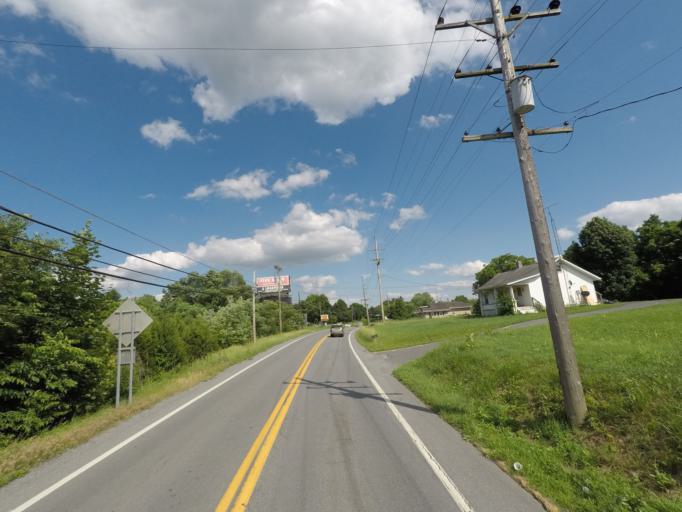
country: US
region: West Virginia
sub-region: Berkeley County
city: Martinsburg
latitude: 39.4222
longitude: -77.9241
